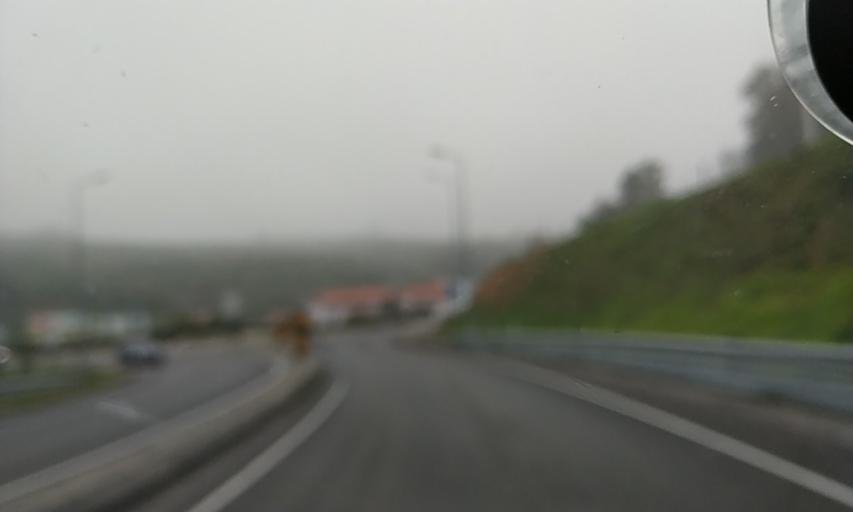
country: PT
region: Viseu
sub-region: Lamego
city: Lamego
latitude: 41.0829
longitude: -7.7975
